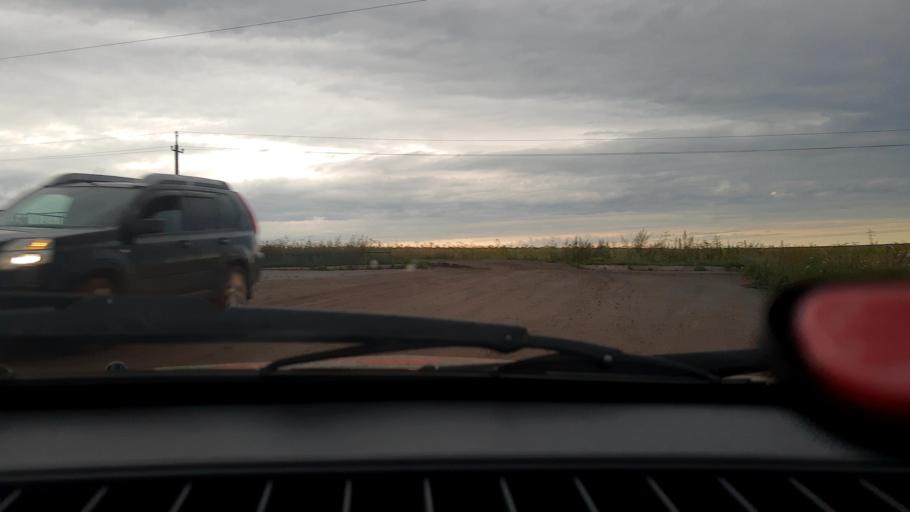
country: RU
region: Bashkortostan
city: Avdon
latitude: 54.7084
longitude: 55.7979
